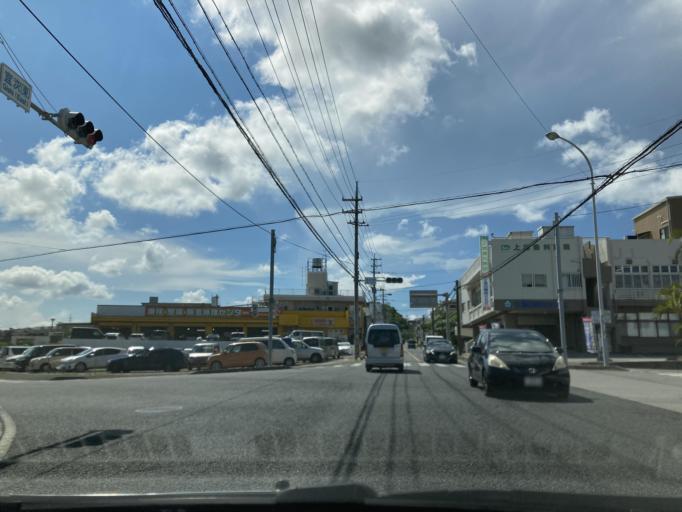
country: JP
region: Okinawa
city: Tomigusuku
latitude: 26.1760
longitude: 127.7188
